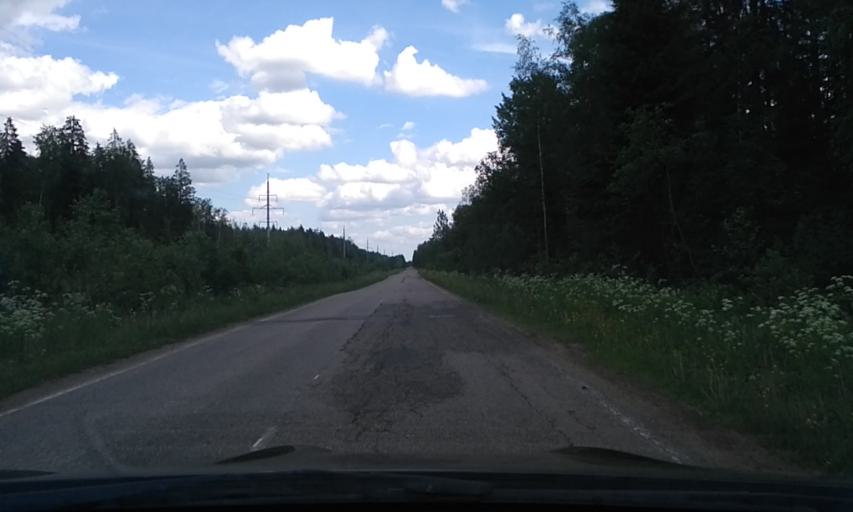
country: RU
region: Leningrad
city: Otradnoye
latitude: 59.8207
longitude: 30.7914
